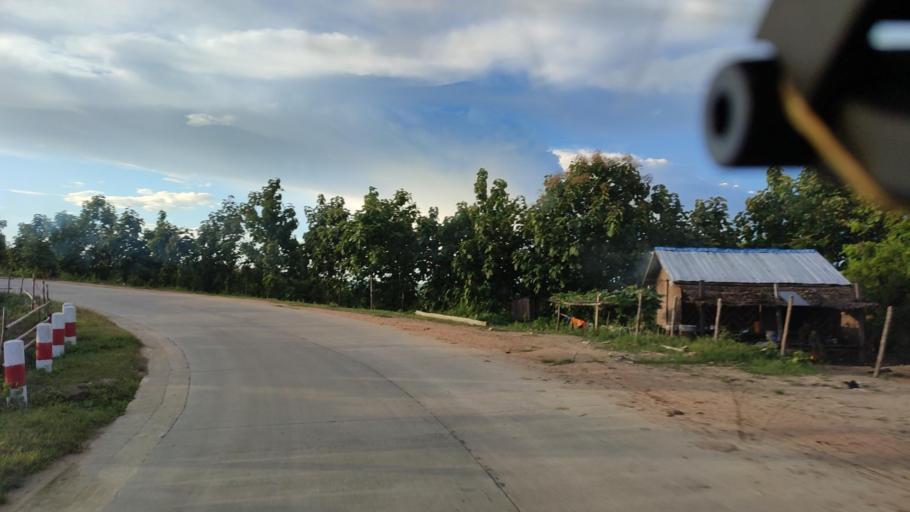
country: MM
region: Magway
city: Taungdwingyi
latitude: 20.0504
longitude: 95.7750
